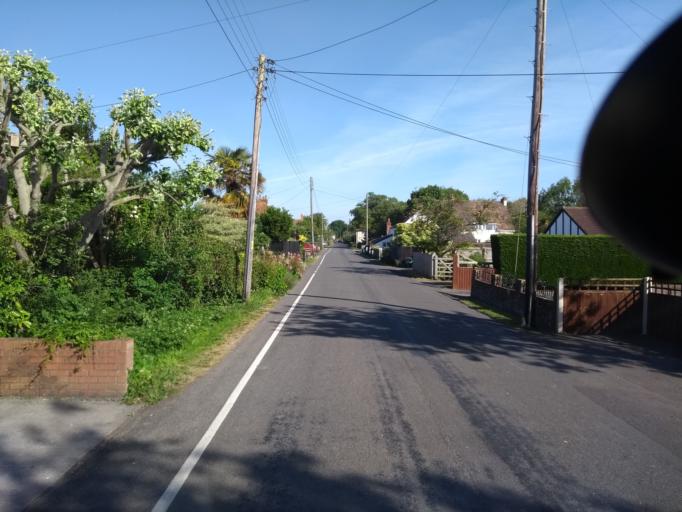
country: GB
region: England
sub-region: Somerset
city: Highbridge
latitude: 51.2460
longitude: -2.9496
